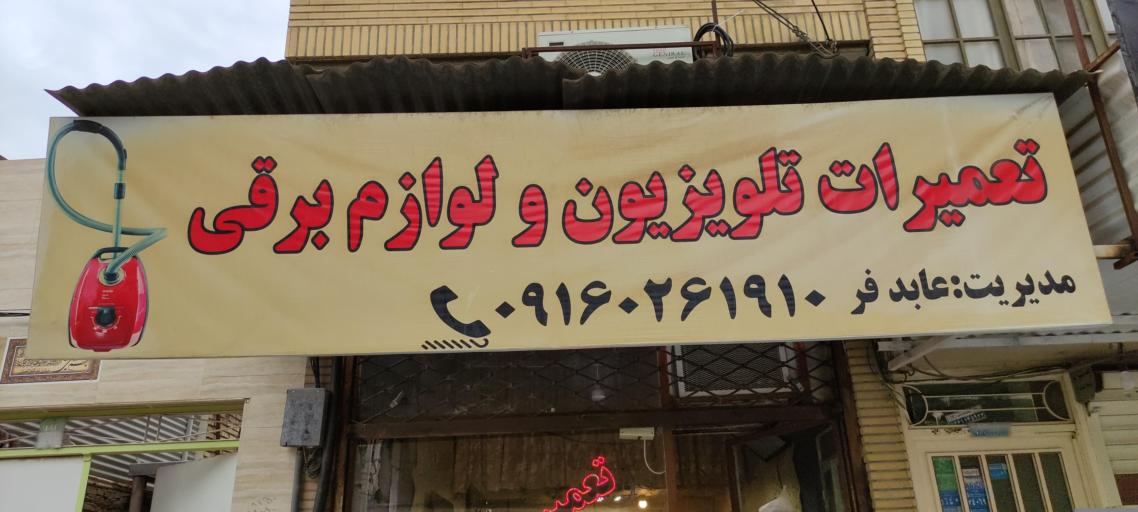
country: IR
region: Khuzestan
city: Dezful
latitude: 32.3748
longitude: 48.4036
